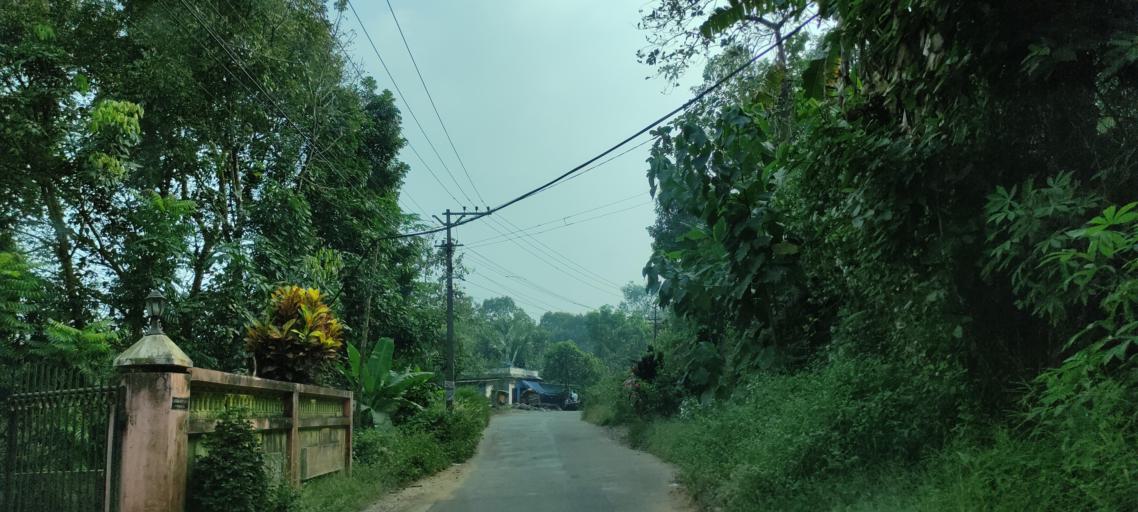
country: IN
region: Kerala
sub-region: Ernakulam
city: Piravam
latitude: 9.8011
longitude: 76.5355
